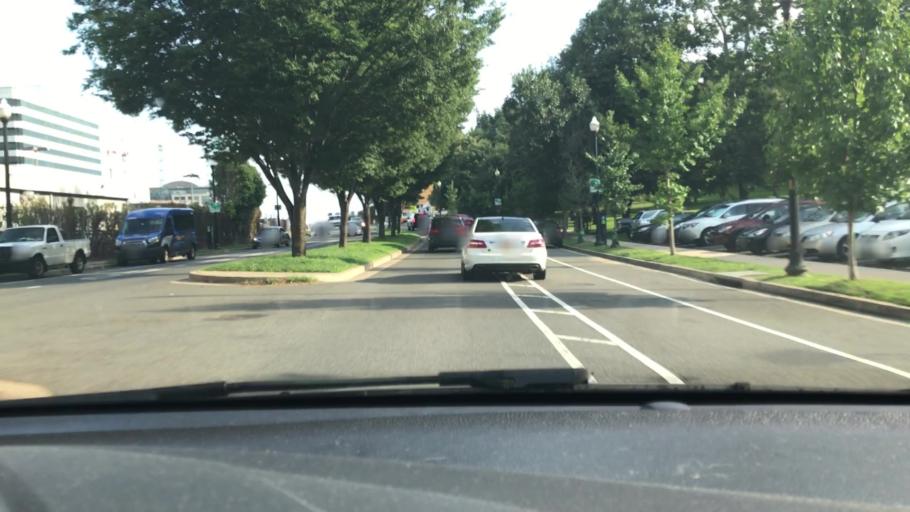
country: US
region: Virginia
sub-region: City of Alexandria
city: Alexandria
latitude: 38.8493
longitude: -77.0538
